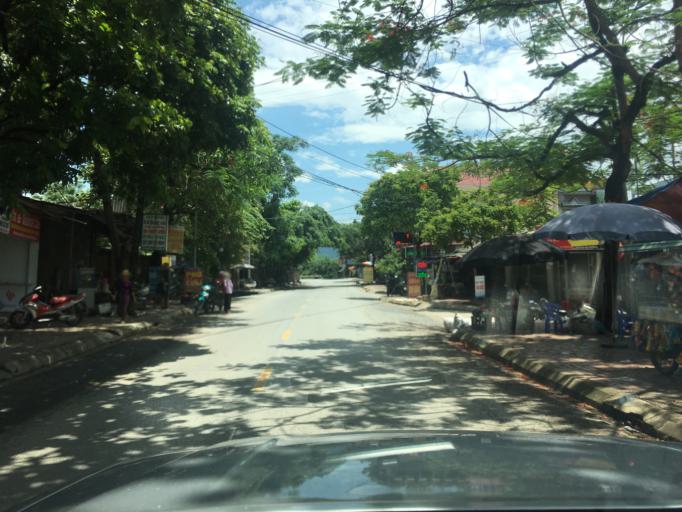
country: VN
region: Yen Bai
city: Son Thinh
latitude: 21.6129
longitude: 104.5065
